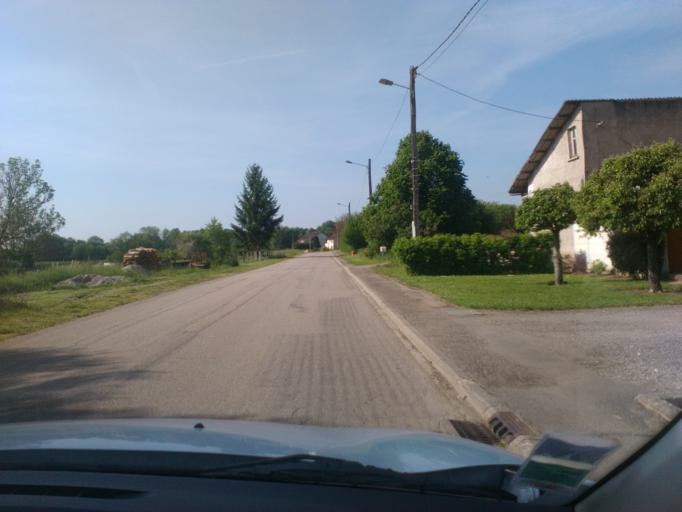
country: FR
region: Lorraine
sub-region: Departement des Vosges
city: Mirecourt
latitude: 48.3453
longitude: 6.1389
